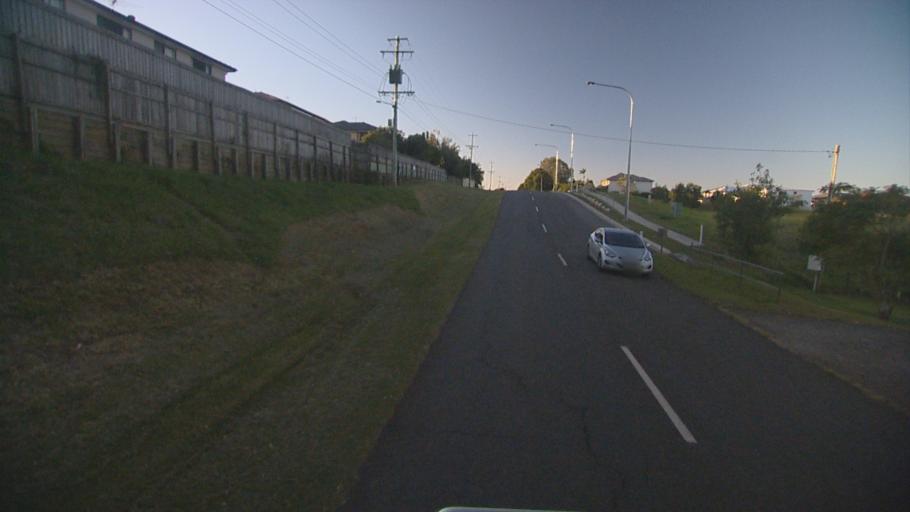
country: AU
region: Queensland
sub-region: Logan
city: Rochedale South
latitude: -27.6030
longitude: 153.1041
